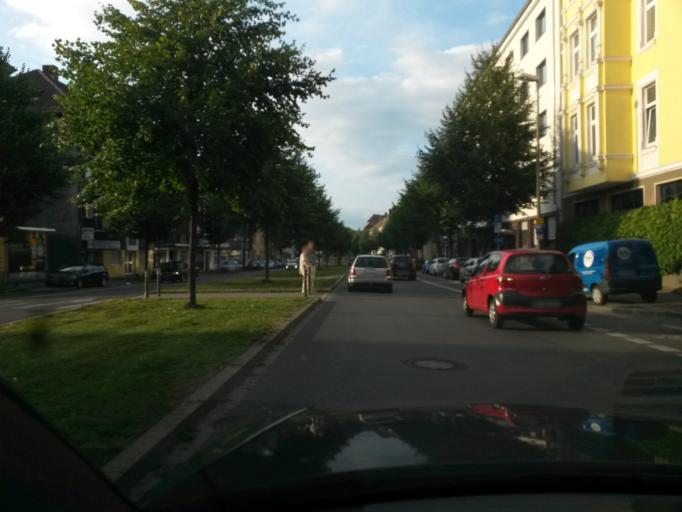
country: DE
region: North Rhine-Westphalia
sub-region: Regierungsbezirk Arnsberg
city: Dortmund
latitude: 51.5154
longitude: 7.4746
